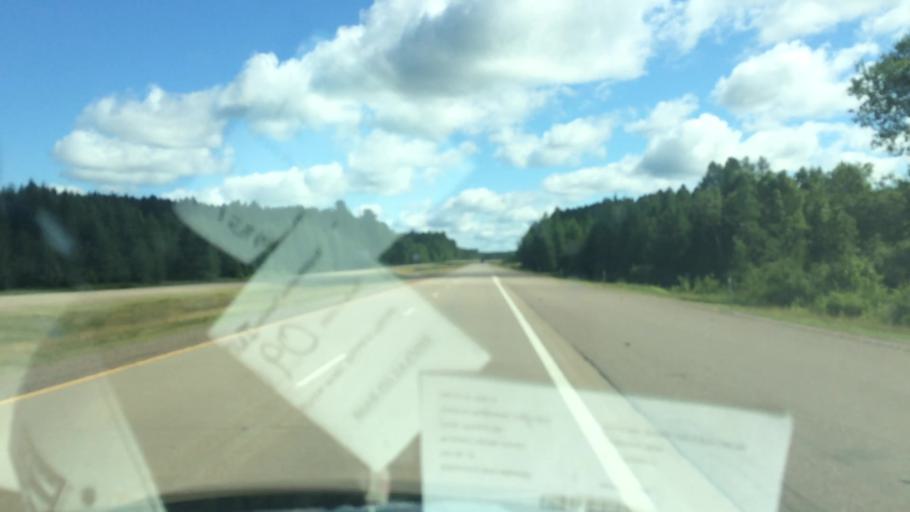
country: US
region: Wisconsin
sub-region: Lincoln County
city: Tomahawk
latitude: 45.5005
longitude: -89.6934
